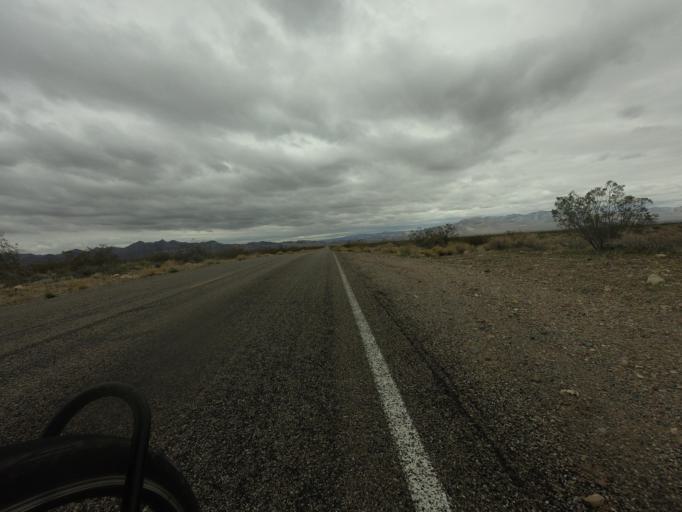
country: US
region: Nevada
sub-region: Nye County
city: Beatty
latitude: 36.8243
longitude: -116.8906
